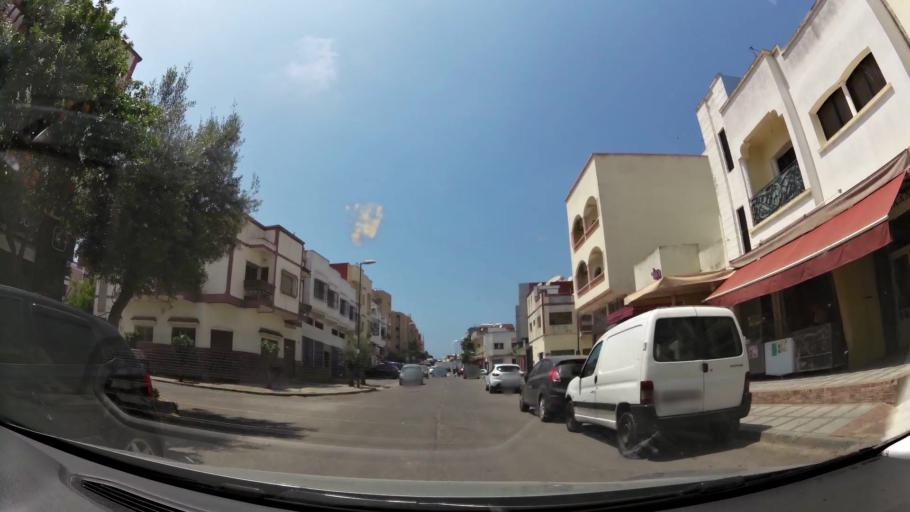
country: MA
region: Rabat-Sale-Zemmour-Zaer
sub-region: Skhirate-Temara
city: Temara
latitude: 33.9741
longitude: -6.8923
